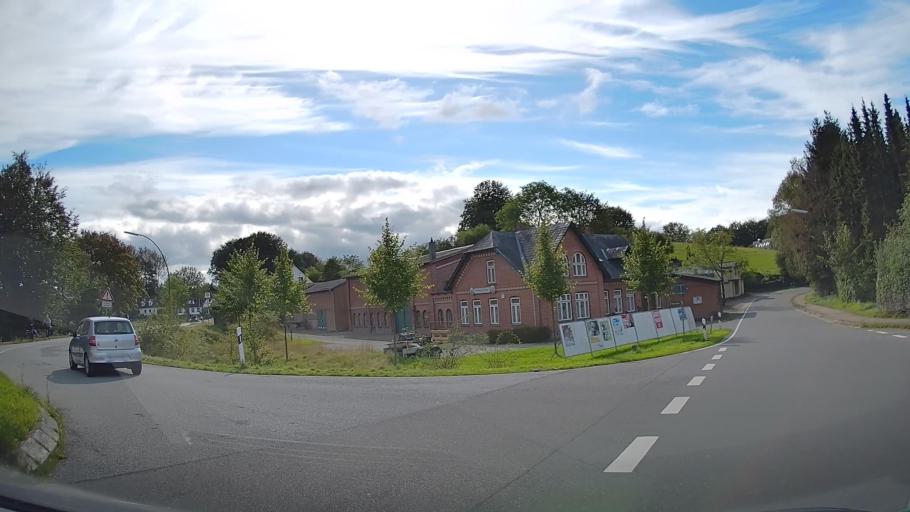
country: DE
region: Schleswig-Holstein
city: Glucksburg
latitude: 54.8442
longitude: 9.5835
